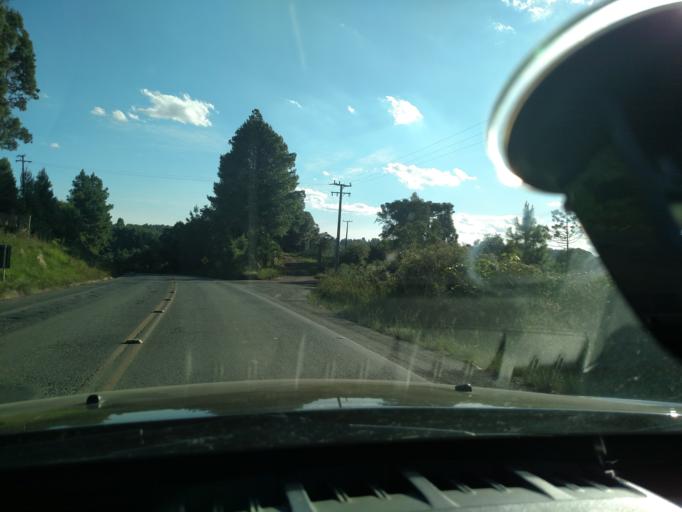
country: BR
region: Santa Catarina
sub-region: Otacilio Costa
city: Otacilio Costa
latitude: -27.5833
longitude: -50.1642
